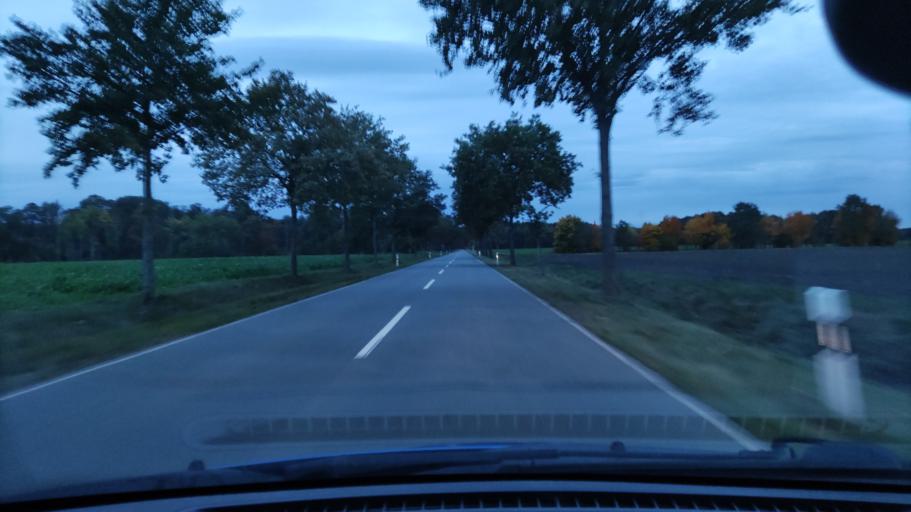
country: DE
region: Lower Saxony
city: Prezelle
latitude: 52.9618
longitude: 11.3914
